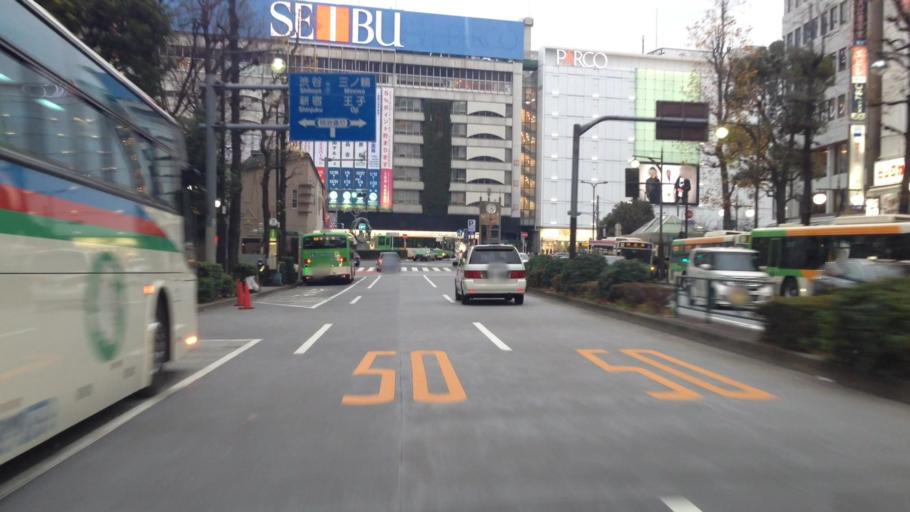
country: JP
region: Tokyo
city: Tokyo
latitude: 35.7294
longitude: 139.7136
